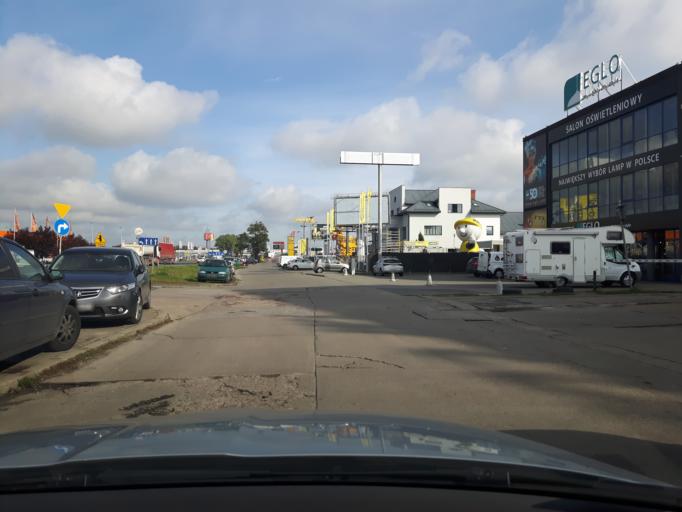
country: PL
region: Masovian Voivodeship
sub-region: Powiat wolominski
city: Zabki
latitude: 52.3008
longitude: 21.0872
